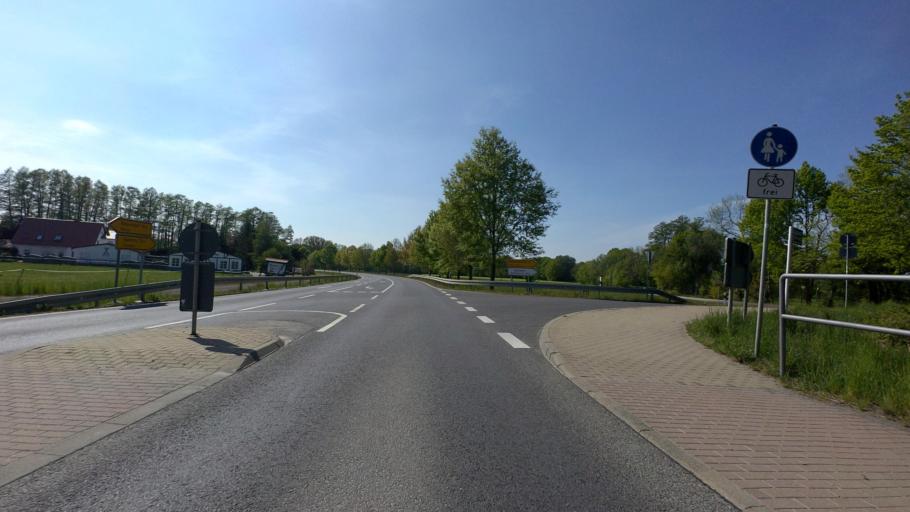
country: DE
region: Saxony
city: Wittichenau
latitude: 51.3880
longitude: 14.2398
